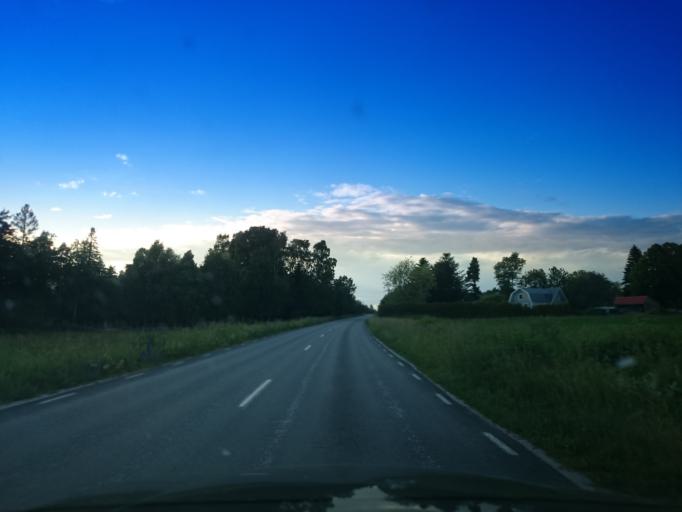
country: SE
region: Gotland
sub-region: Gotland
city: Hemse
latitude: 57.3274
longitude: 18.3810
